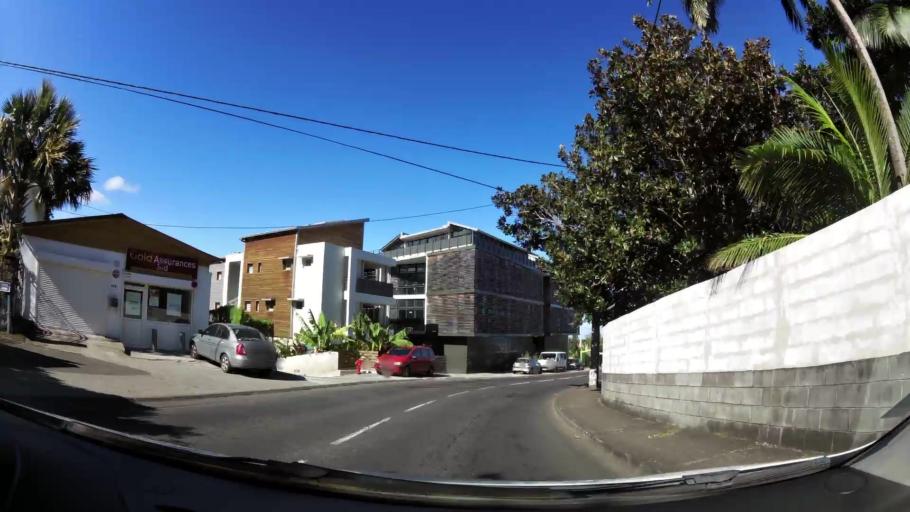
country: RE
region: Reunion
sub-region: Reunion
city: Le Tampon
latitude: -21.2824
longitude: 55.5243
